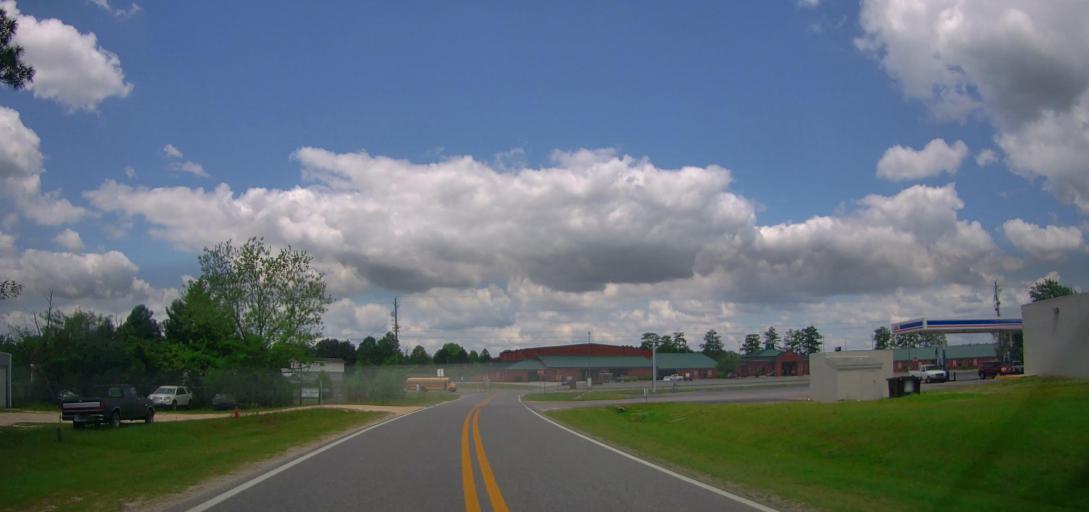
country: US
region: Georgia
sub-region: Laurens County
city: East Dublin
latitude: 32.5597
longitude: -82.8201
